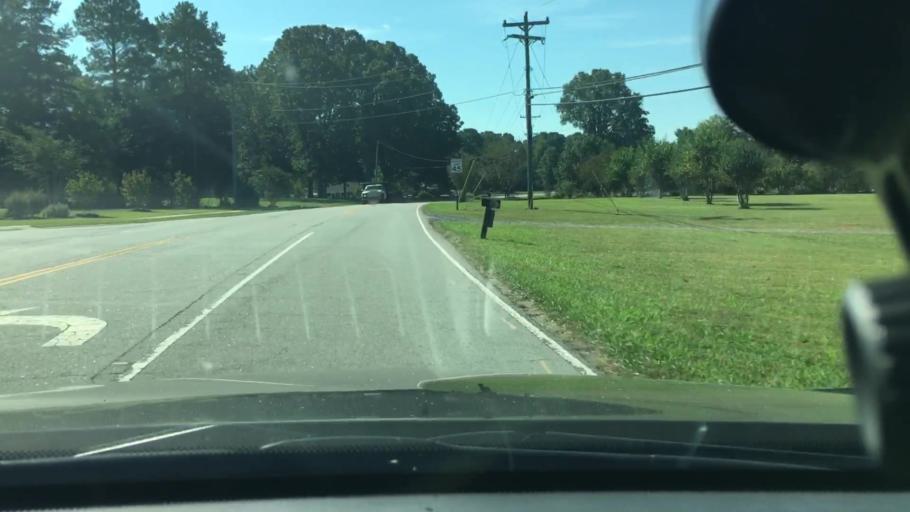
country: US
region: North Carolina
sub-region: Gaston County
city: Mount Holly
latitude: 35.2647
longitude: -80.9754
